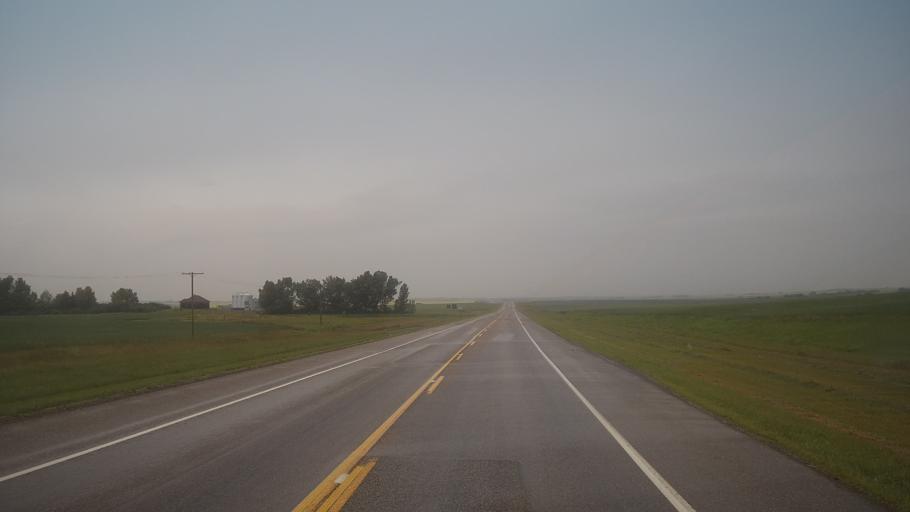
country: CA
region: Saskatchewan
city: Wilkie
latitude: 52.2038
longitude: -108.4747
